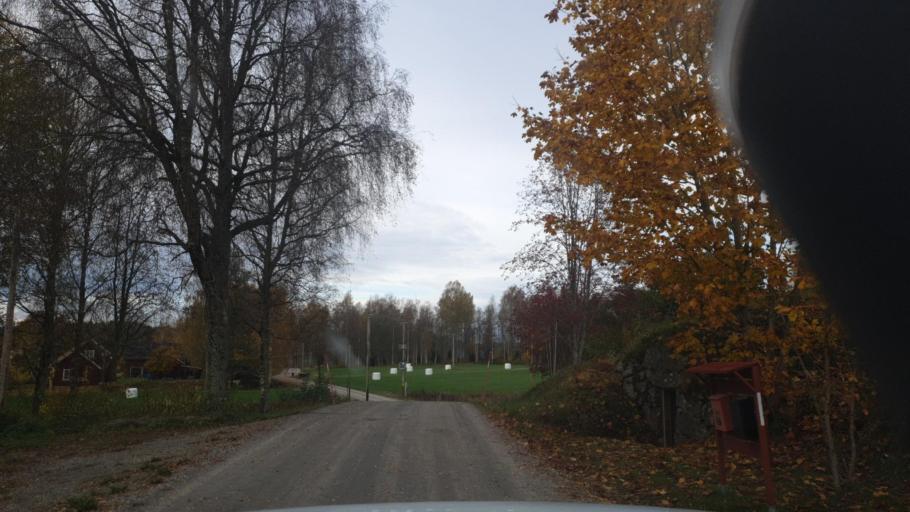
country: SE
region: Vaermland
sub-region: Arvika Kommun
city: Arvika
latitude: 59.7162
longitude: 12.8443
